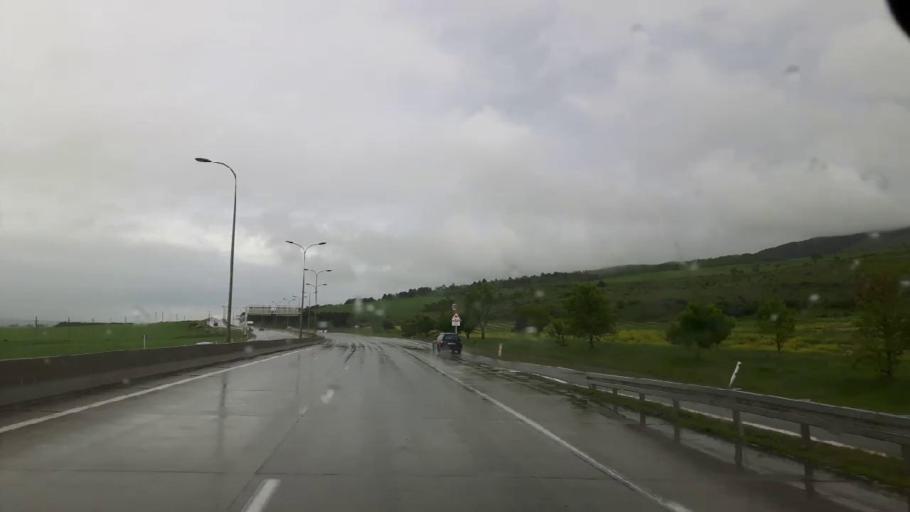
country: GE
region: Shida Kartli
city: Gori
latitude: 42.0257
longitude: 44.2094
